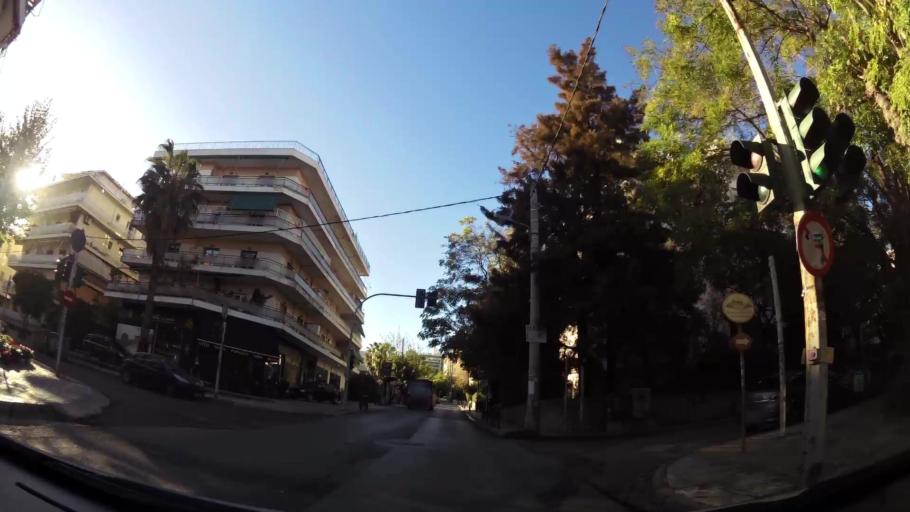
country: GR
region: Attica
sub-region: Nomarchia Athinas
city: Marousi
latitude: 38.0581
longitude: 23.8012
